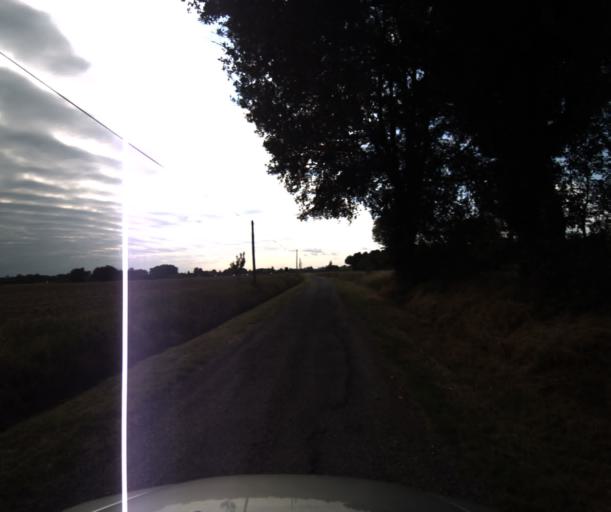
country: FR
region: Midi-Pyrenees
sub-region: Departement de la Haute-Garonne
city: Eaunes
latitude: 43.4319
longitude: 1.3152
